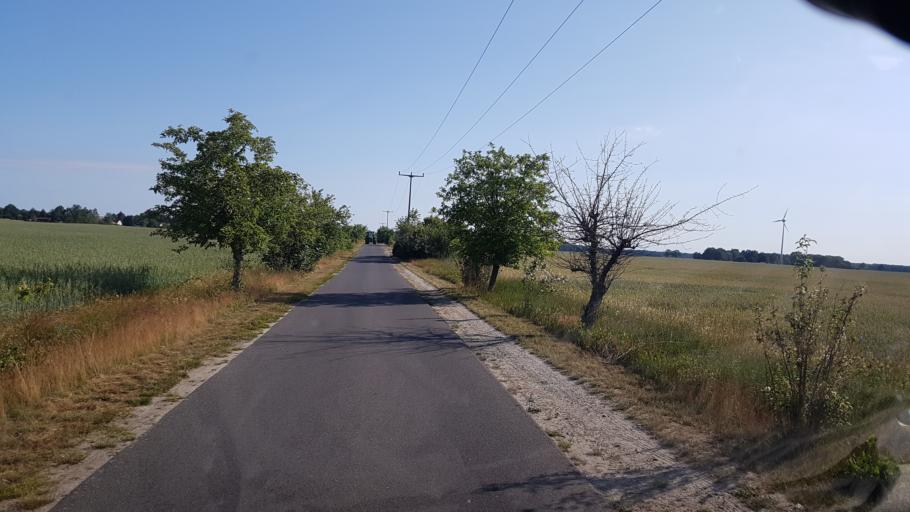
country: DE
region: Brandenburg
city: Sallgast
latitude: 51.5981
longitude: 13.8588
